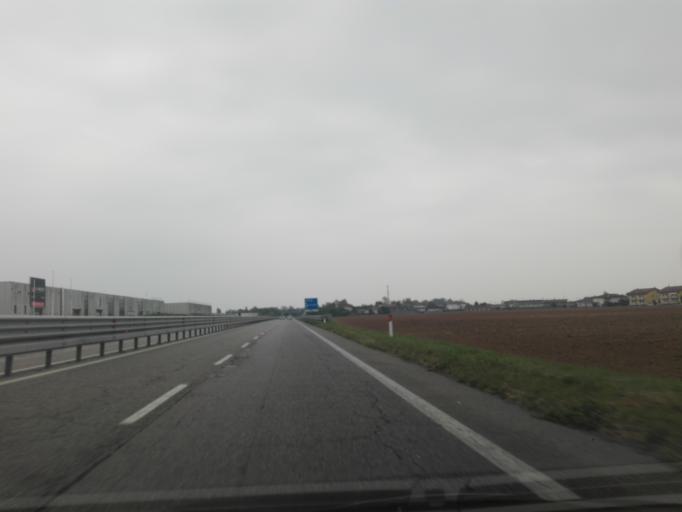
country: IT
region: Veneto
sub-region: Provincia di Verona
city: Isola Rizza
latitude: 45.2840
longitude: 11.1982
